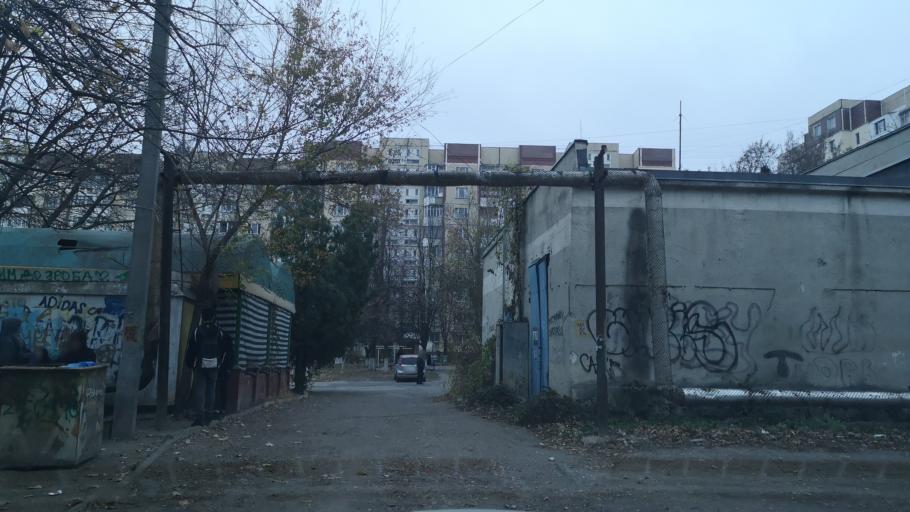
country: MD
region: Chisinau
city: Chisinau
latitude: 46.9759
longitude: 28.8684
